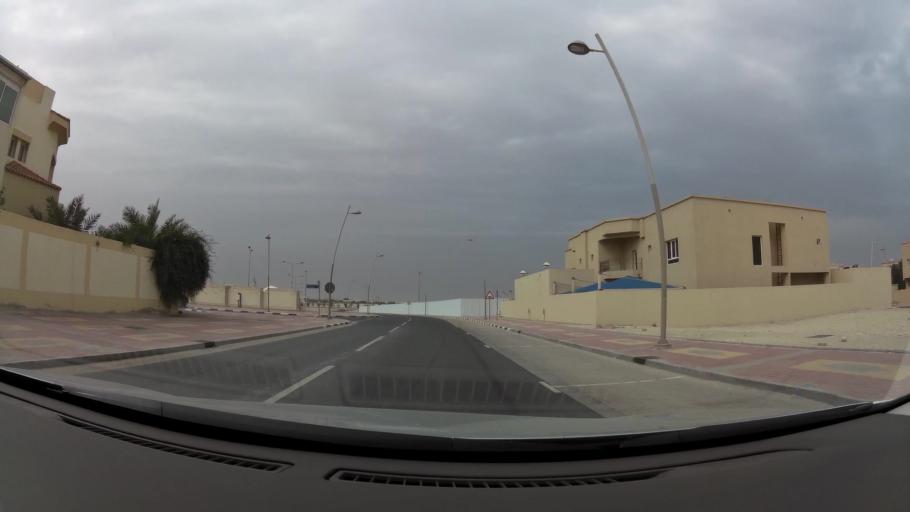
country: QA
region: Baladiyat ad Dawhah
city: Doha
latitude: 25.3461
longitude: 51.4855
